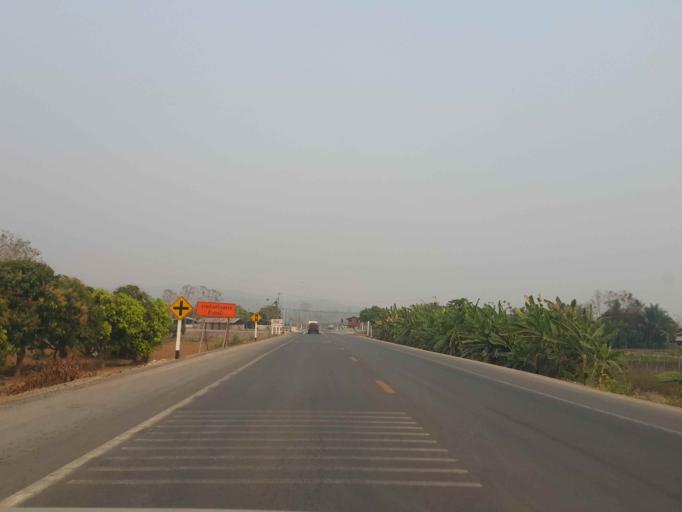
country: TH
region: Chiang Mai
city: Mae Taeng
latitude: 19.0712
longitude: 98.9505
